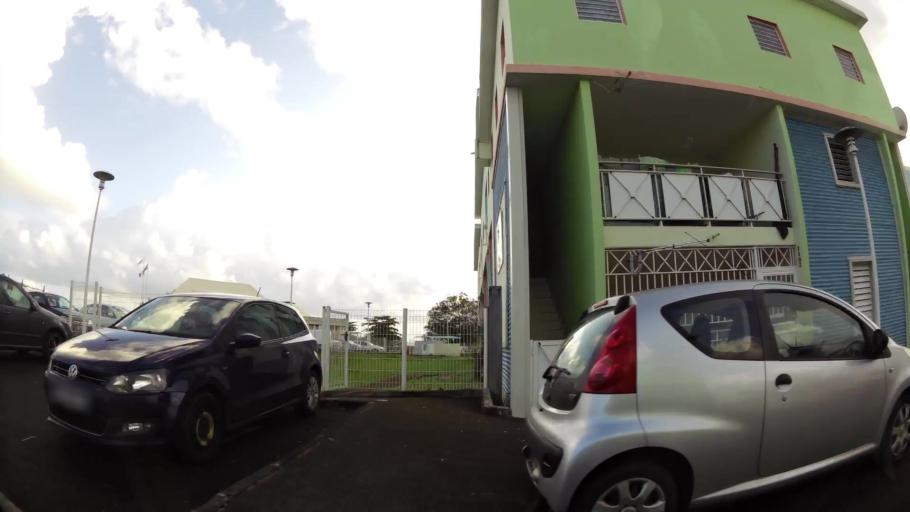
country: GP
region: Guadeloupe
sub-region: Guadeloupe
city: Petit-Bourg
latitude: 16.1326
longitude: -61.5756
